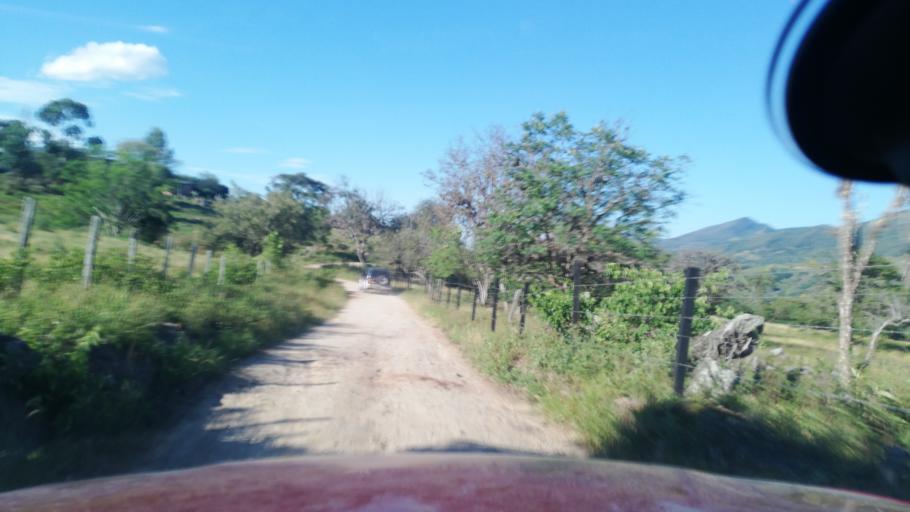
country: CO
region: Cundinamarca
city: Viani
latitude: 4.8176
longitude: -74.6167
